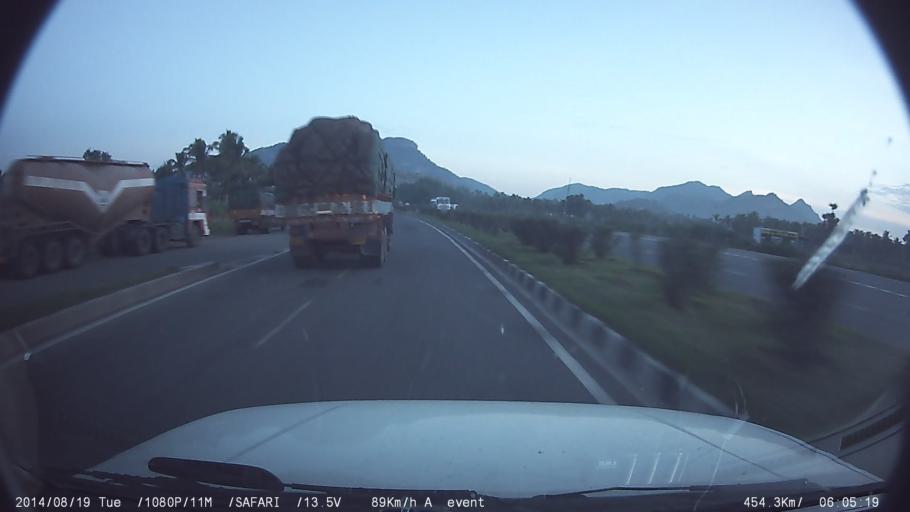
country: IN
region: Tamil Nadu
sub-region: Salem
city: Omalur
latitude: 11.8772
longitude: 78.0823
